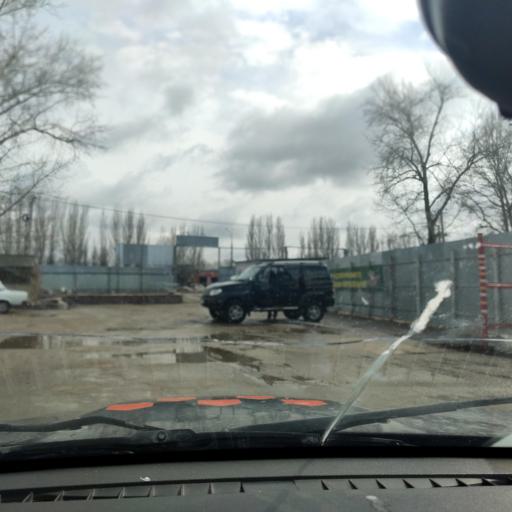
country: RU
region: Samara
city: Tol'yatti
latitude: 53.5408
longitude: 49.2774
